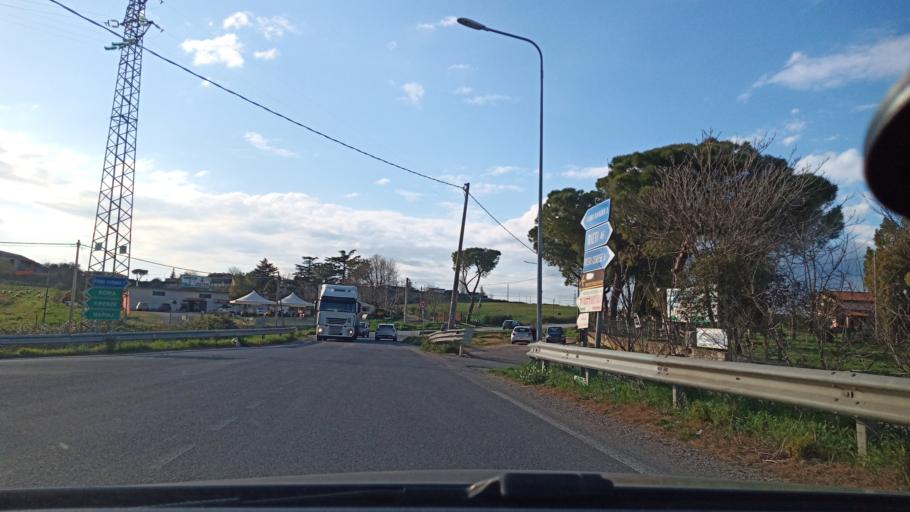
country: IT
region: Latium
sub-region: Citta metropolitana di Roma Capitale
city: Fiano Romano
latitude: 42.1481
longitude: 12.6188
